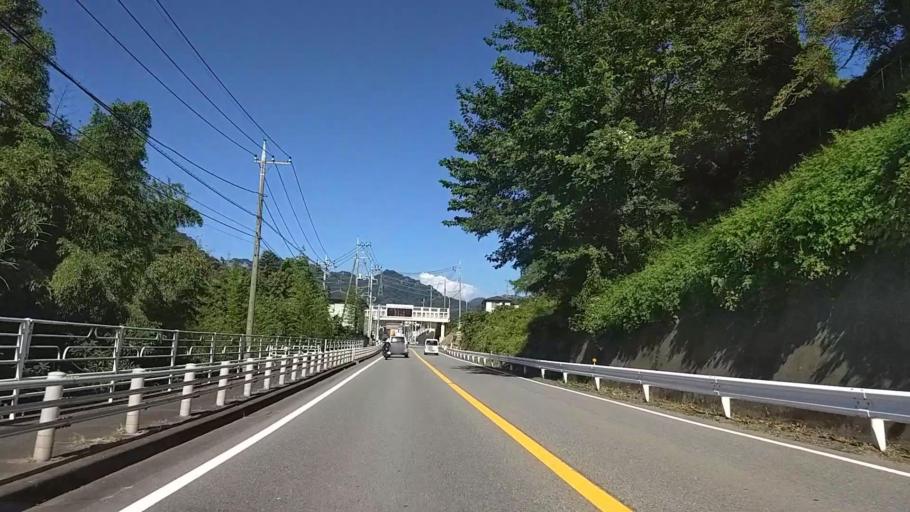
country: JP
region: Gunma
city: Annaka
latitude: 36.3344
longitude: 138.7430
